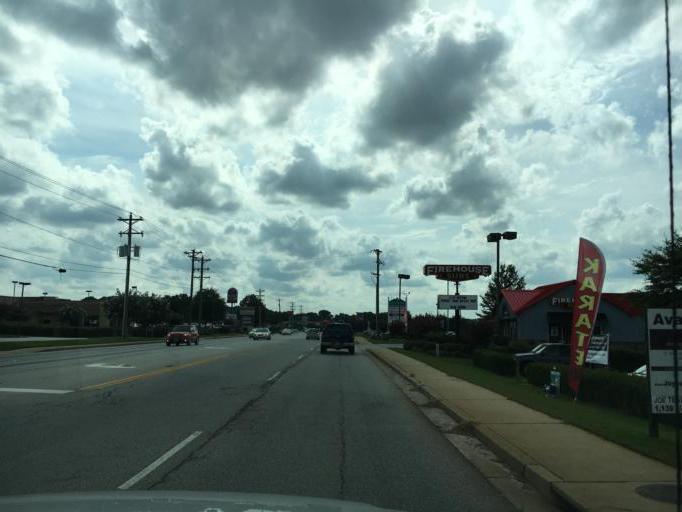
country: US
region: South Carolina
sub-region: Greenville County
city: Five Forks
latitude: 34.8198
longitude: -82.2695
